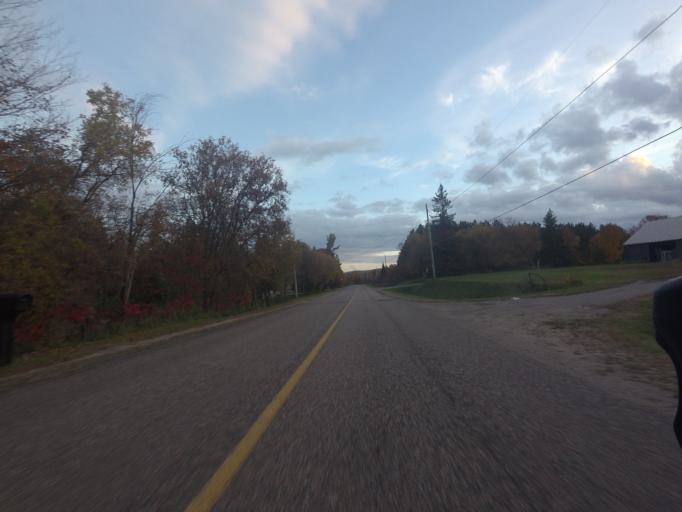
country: CA
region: Ontario
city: Renfrew
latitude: 45.3950
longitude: -76.9504
